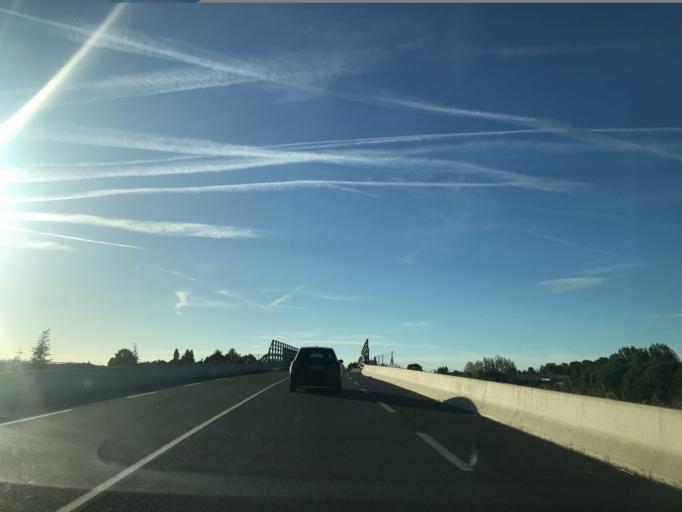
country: FR
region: Poitou-Charentes
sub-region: Departement de la Charente-Maritime
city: Montguyon
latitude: 45.2092
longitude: -0.1667
